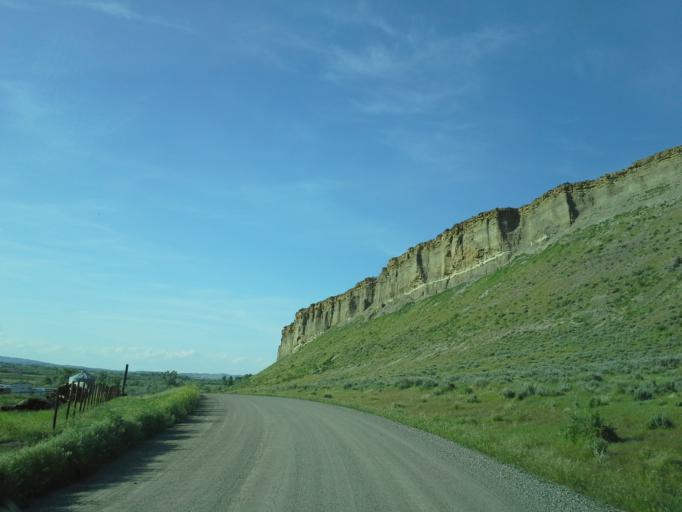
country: US
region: Wyoming
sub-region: Hot Springs County
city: Thermopolis
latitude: 43.6864
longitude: -108.1632
